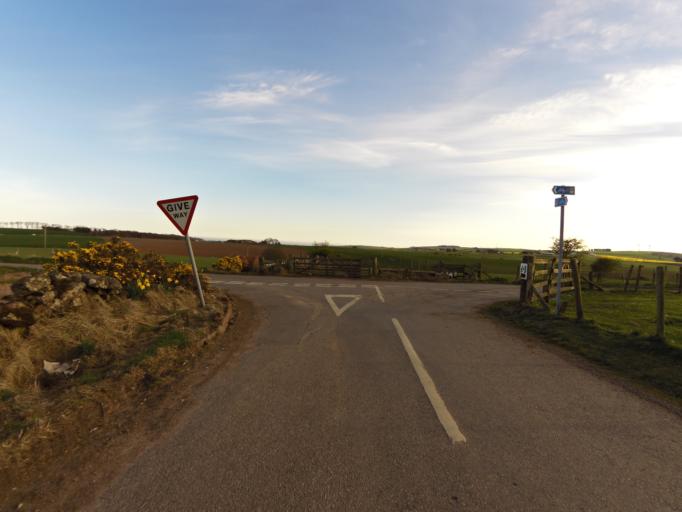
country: GB
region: Scotland
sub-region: Aberdeenshire
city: Stonehaven
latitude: 56.9129
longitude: -2.2272
